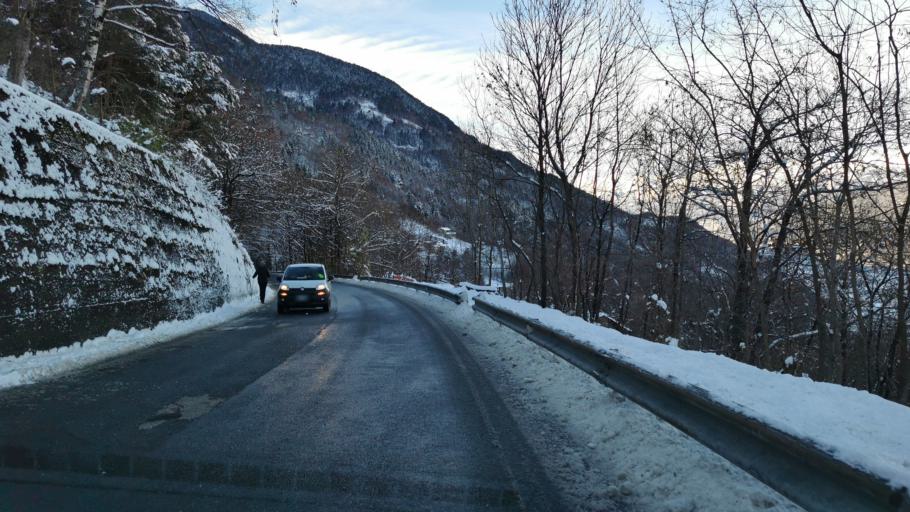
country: IT
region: Lombardy
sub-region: Provincia di Sondrio
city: Regoledo
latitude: 46.1238
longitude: 9.5455
